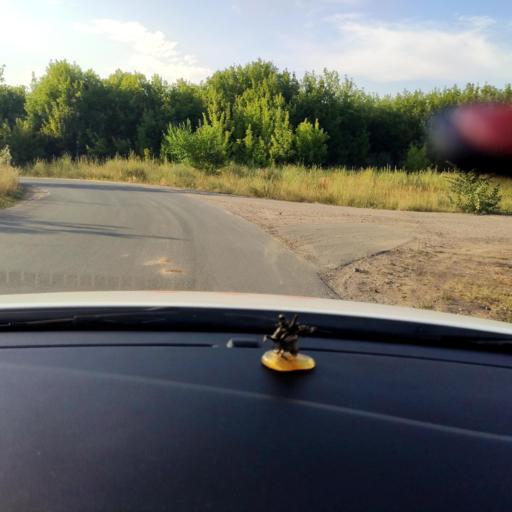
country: RU
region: Tatarstan
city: Staroye Arakchino
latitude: 55.8142
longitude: 48.9116
